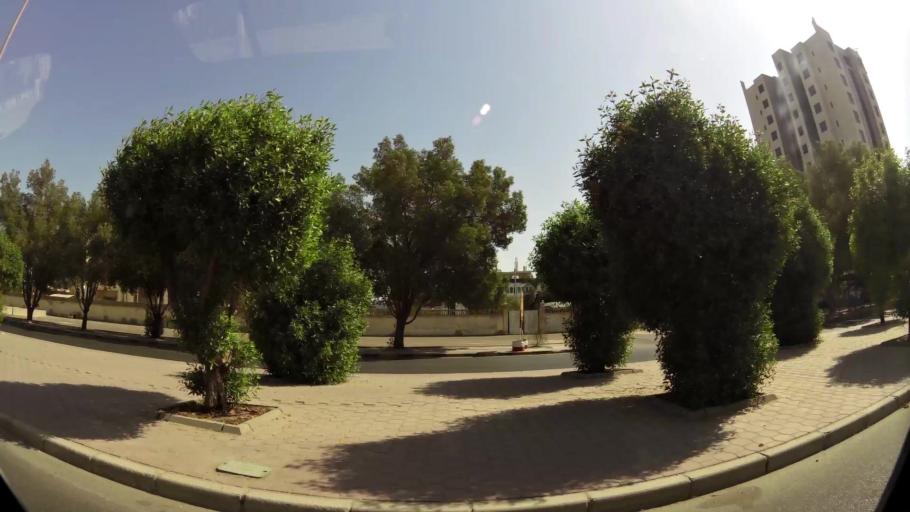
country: KW
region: Al Asimah
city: Ad Dasmah
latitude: 29.3825
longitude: 47.9942
